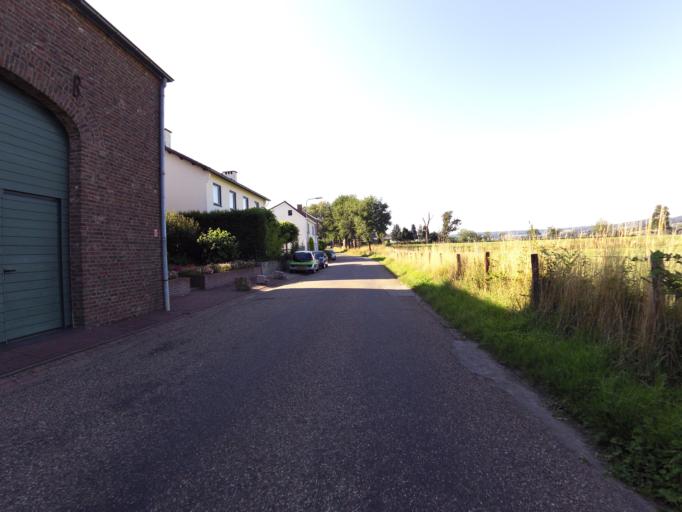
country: BE
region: Wallonia
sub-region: Province de Liege
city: Plombieres
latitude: 50.7915
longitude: 5.9274
